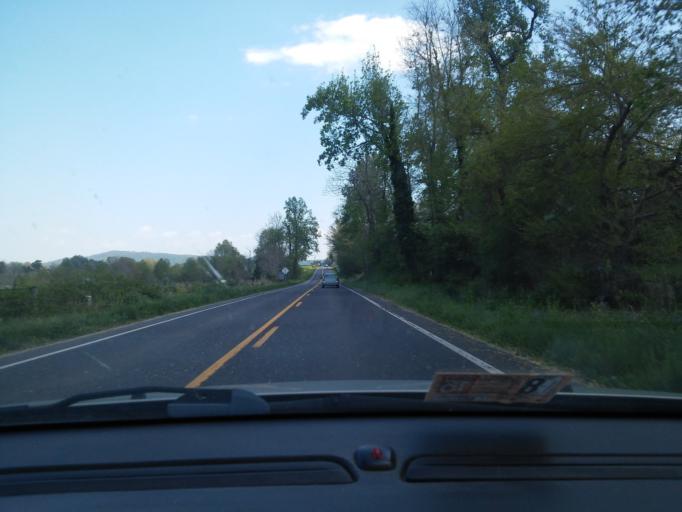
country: US
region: Virginia
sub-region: Rappahannock County
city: Washington
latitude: 38.6551
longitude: -78.2228
